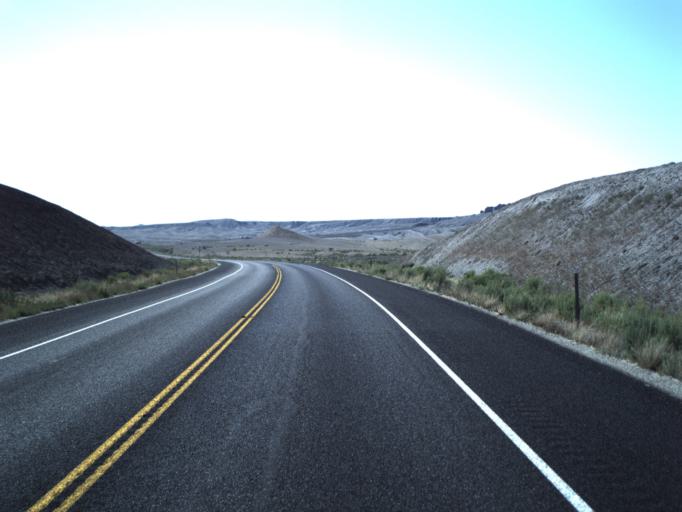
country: US
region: Utah
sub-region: Emery County
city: Ferron
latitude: 39.0634
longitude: -111.1311
